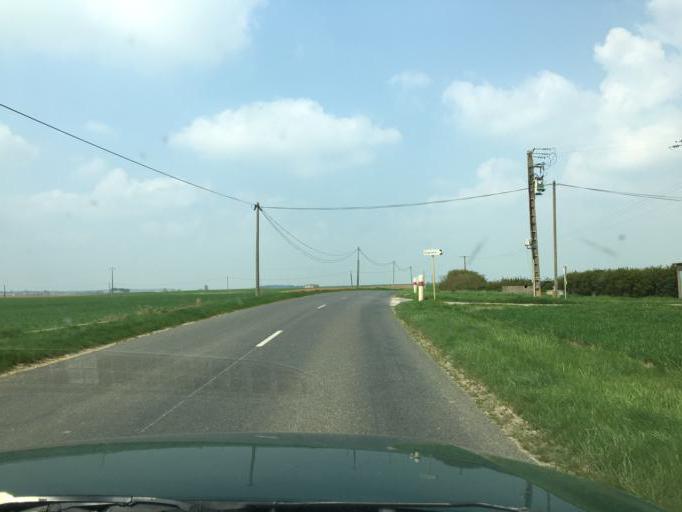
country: FR
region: Centre
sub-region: Departement du Loir-et-Cher
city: Ouzouer-le-Marche
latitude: 47.8437
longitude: 1.5356
